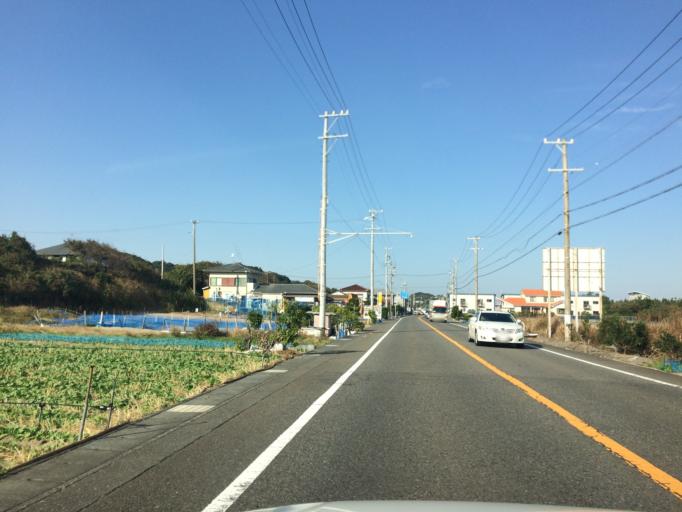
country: JP
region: Shizuoka
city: Sagara
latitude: 34.6609
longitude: 138.1937
